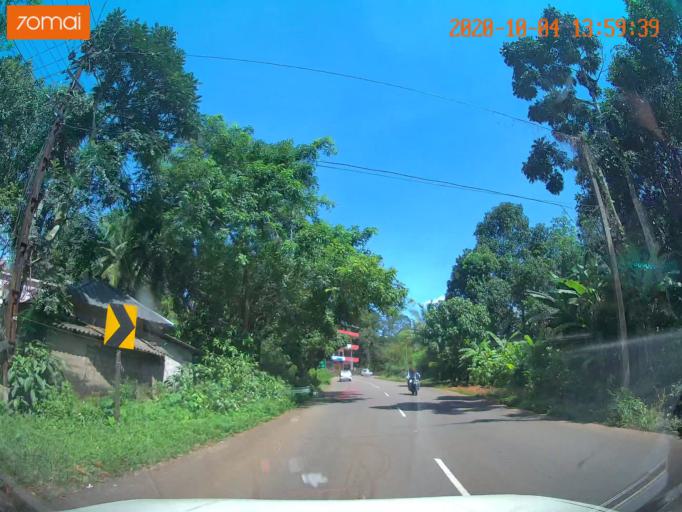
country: IN
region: Kerala
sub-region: Kottayam
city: Lalam
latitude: 9.7165
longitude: 76.6642
